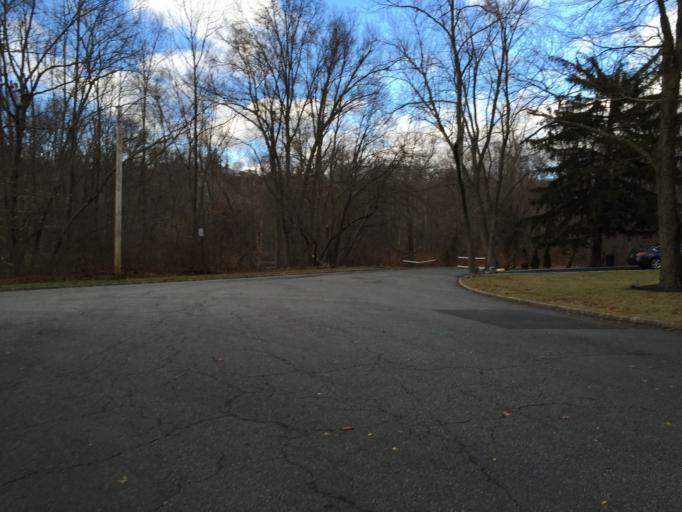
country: US
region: New Jersey
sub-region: Union County
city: New Providence
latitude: 40.7069
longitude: -74.4133
